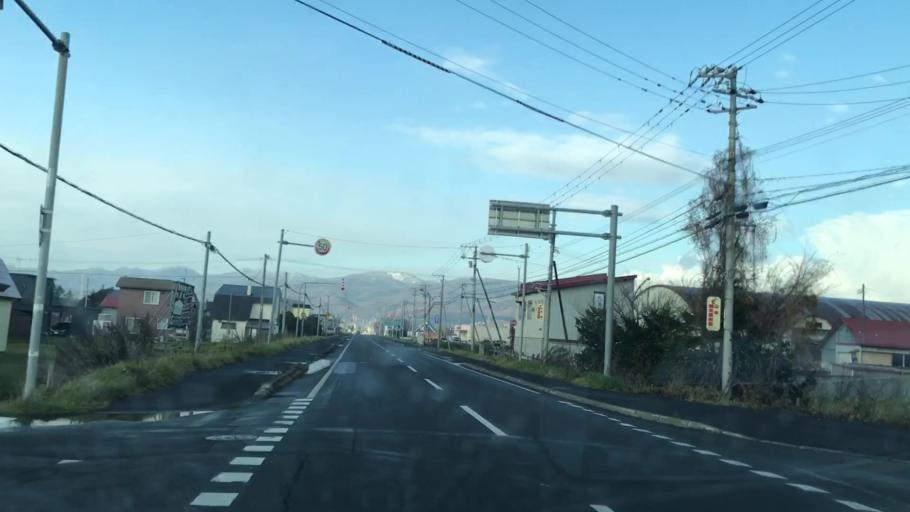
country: JP
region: Hokkaido
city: Yoichi
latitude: 43.1828
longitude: 140.8125
